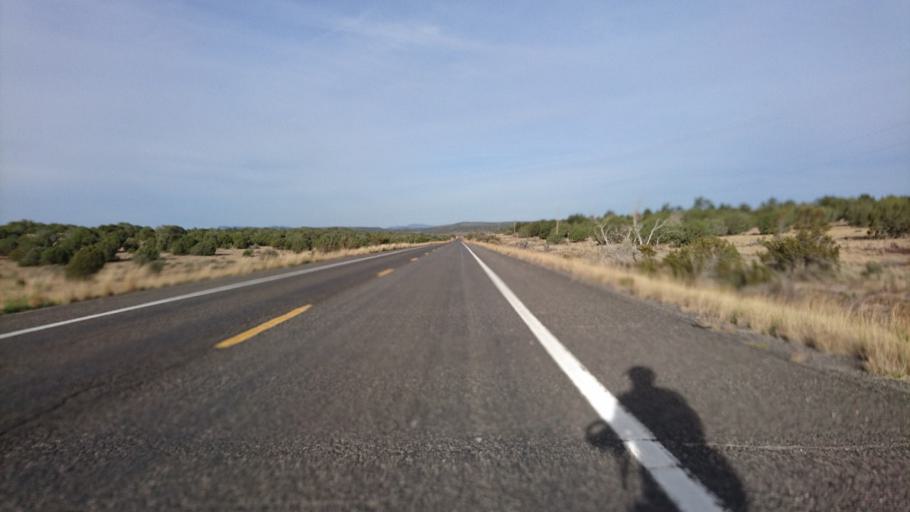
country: US
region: Arizona
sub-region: Mohave County
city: Peach Springs
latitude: 35.5482
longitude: -113.2975
